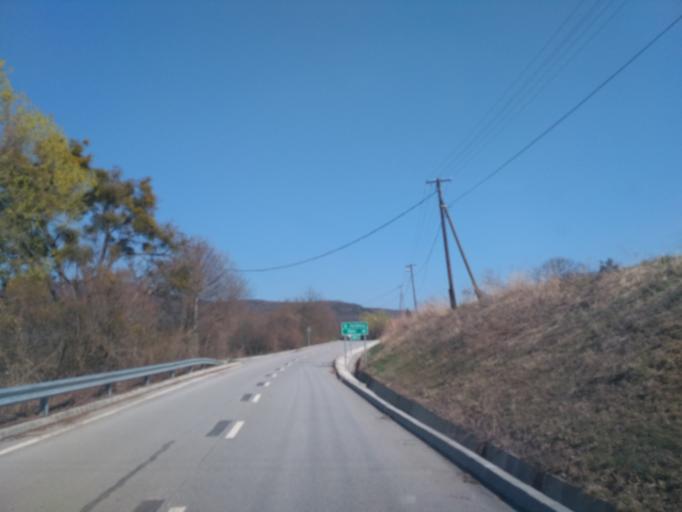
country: HU
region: Borsod-Abauj-Zemplen
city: Gonc
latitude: 48.5452
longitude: 21.3416
